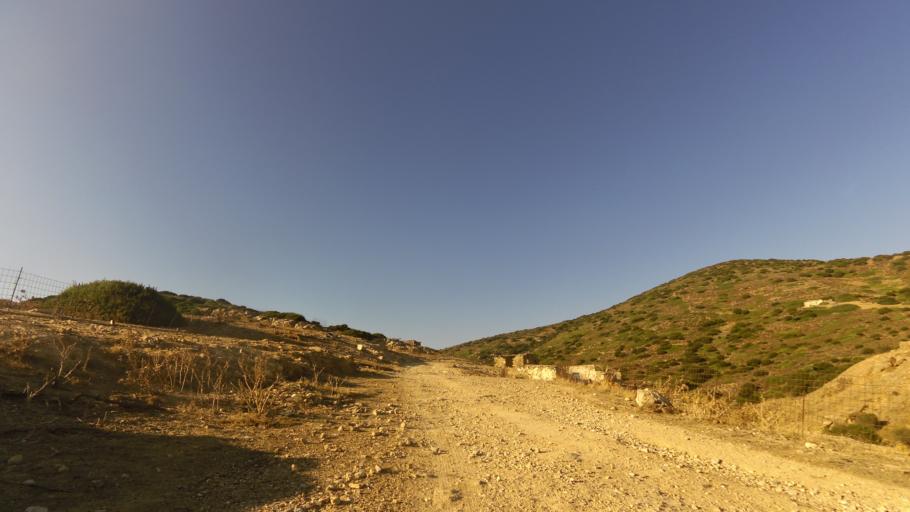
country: GR
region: South Aegean
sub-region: Nomos Kykladon
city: Antiparos
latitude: 36.9846
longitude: 25.0290
